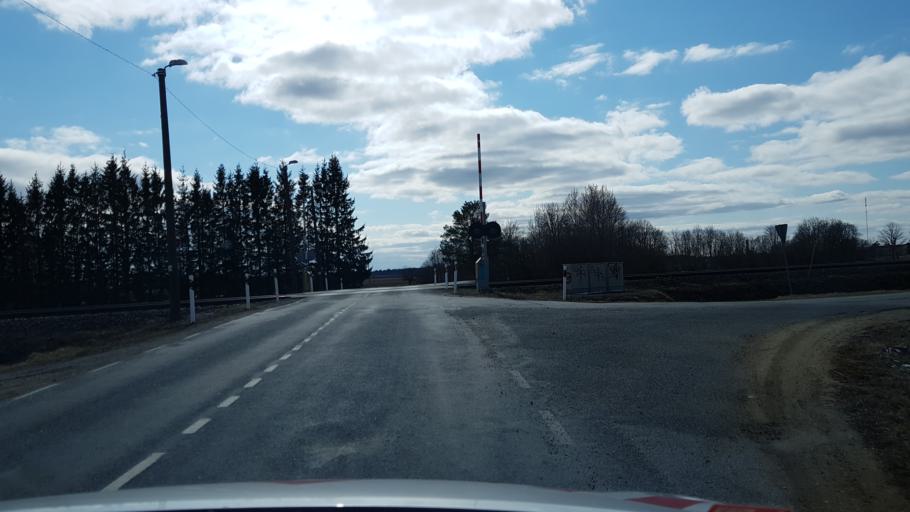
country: EE
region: Laeaene-Virumaa
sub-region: Tapa vald
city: Tapa
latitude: 59.2561
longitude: 25.8405
